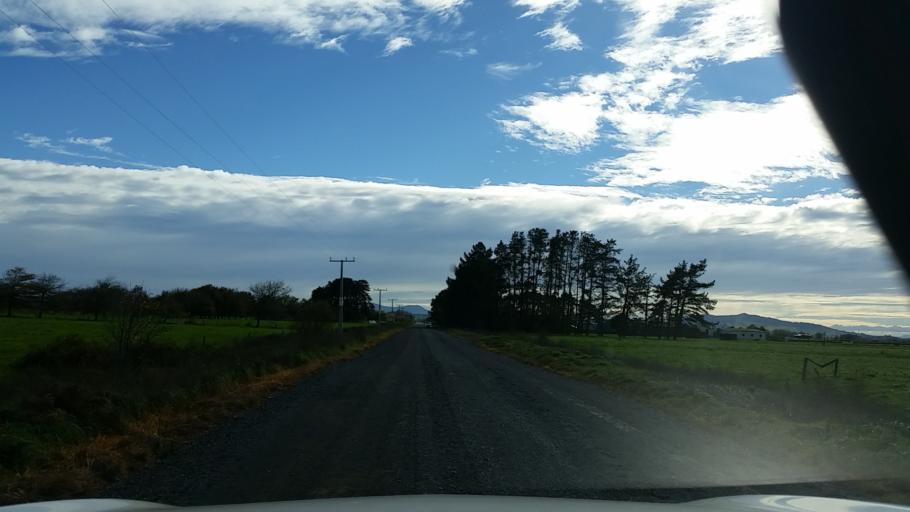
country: NZ
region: Waikato
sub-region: Hamilton City
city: Hamilton
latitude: -37.6604
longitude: 175.4372
